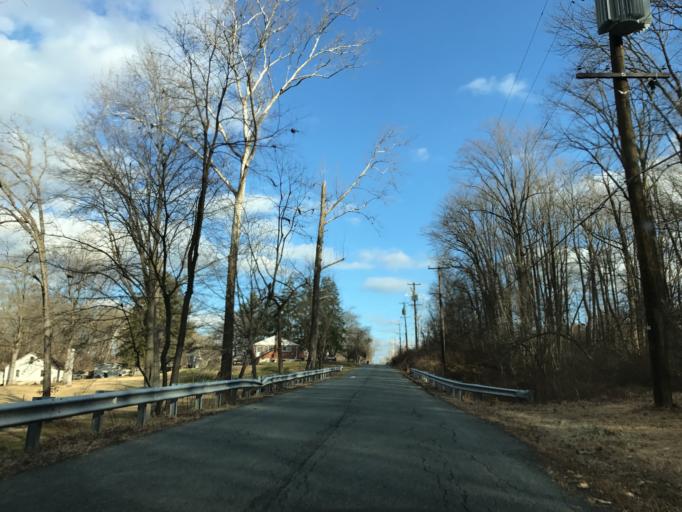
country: US
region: Maryland
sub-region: Cecil County
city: Rising Sun
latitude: 39.6938
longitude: -76.1216
